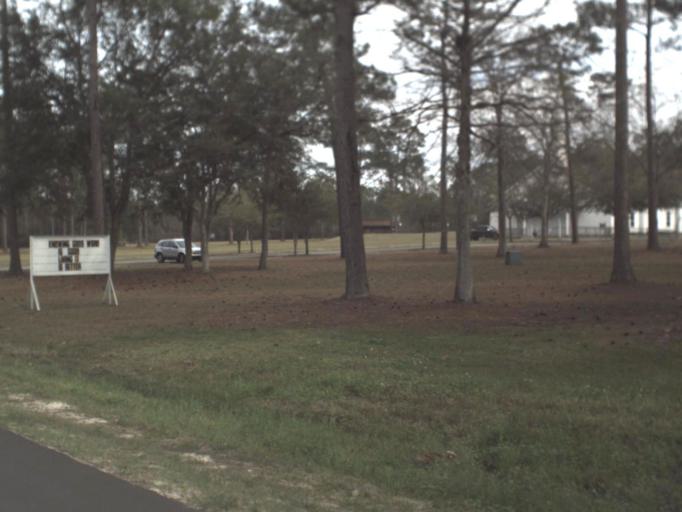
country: US
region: Florida
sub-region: Gadsden County
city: Midway
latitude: 30.3968
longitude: -84.6059
